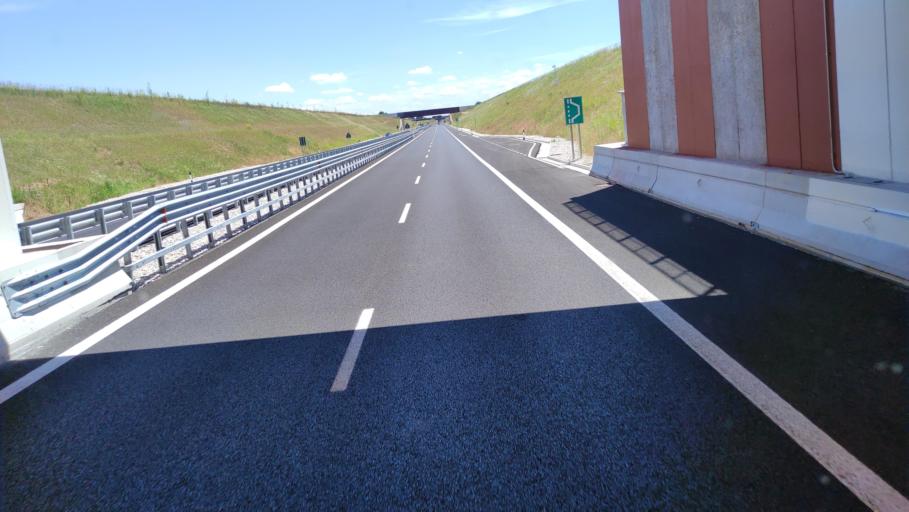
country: IT
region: Veneto
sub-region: Provincia di Treviso
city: Riese Pio X
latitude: 45.7425
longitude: 11.9347
